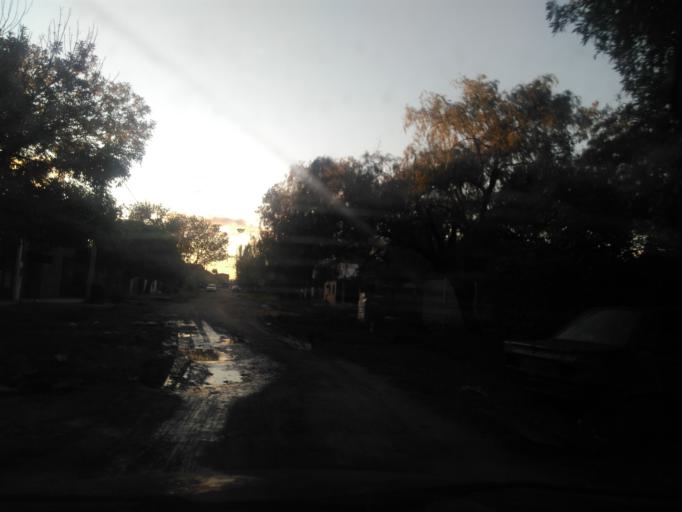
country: AR
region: Chaco
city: Resistencia
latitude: -27.4607
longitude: -59.0078
